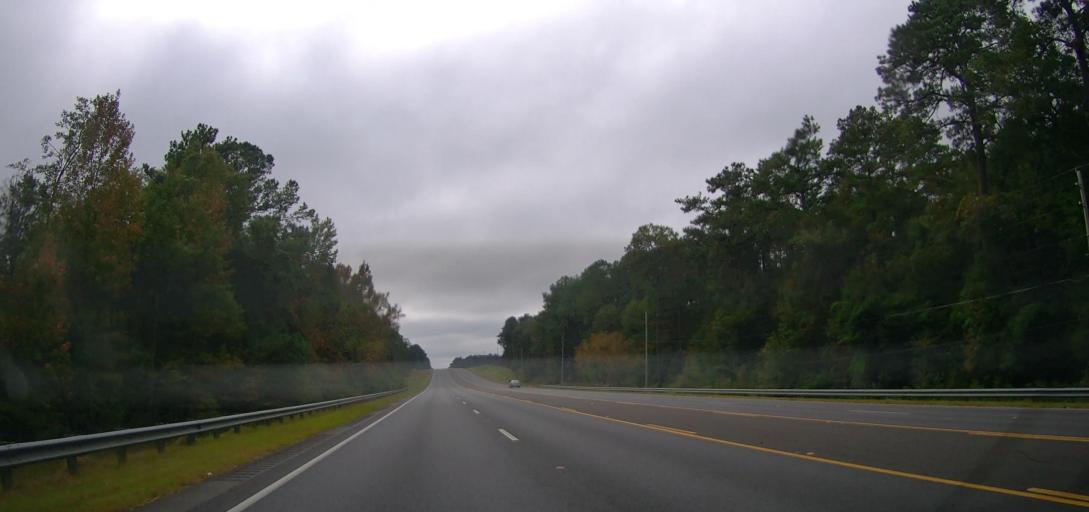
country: US
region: Georgia
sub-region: Thomas County
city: Thomasville
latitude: 30.9203
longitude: -83.9151
